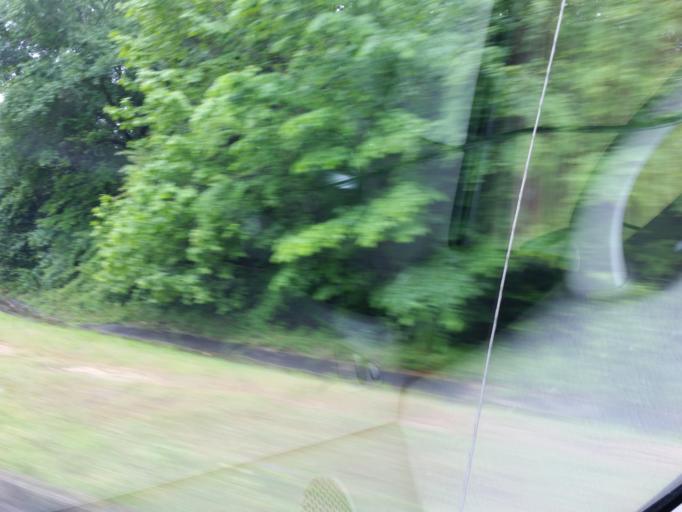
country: US
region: Georgia
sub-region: Peach County
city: Byron
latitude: 32.6515
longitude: -83.7644
